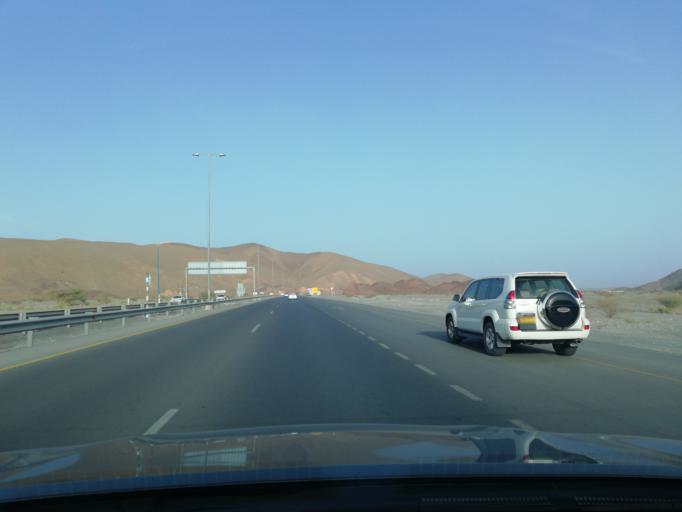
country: OM
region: Muhafazat ad Dakhiliyah
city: Izki
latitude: 22.8906
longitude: 57.6849
